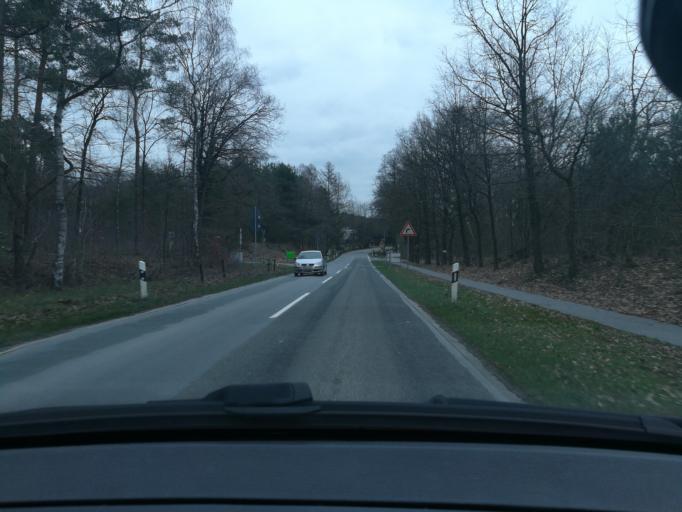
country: DE
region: North Rhine-Westphalia
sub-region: Regierungsbezirk Detmold
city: Oerlinghausen
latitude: 51.9487
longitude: 8.6319
